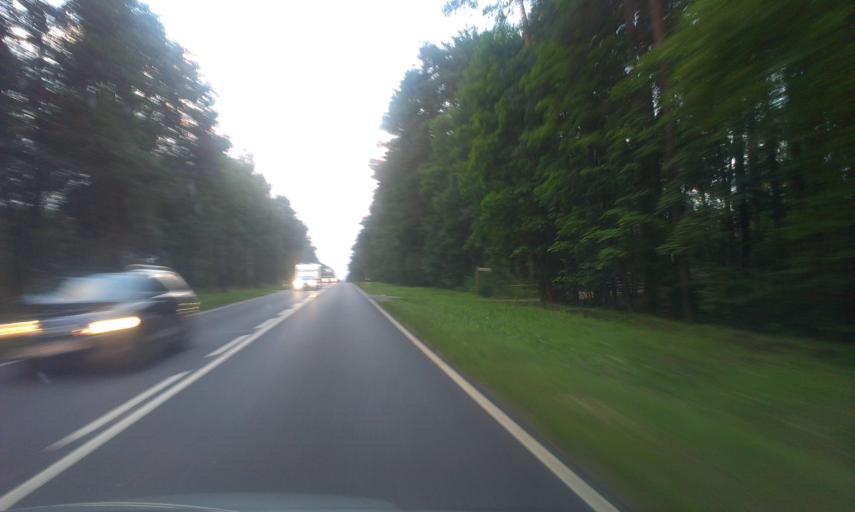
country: PL
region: West Pomeranian Voivodeship
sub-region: Powiat koszalinski
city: Sianow
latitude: 54.1130
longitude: 16.3254
